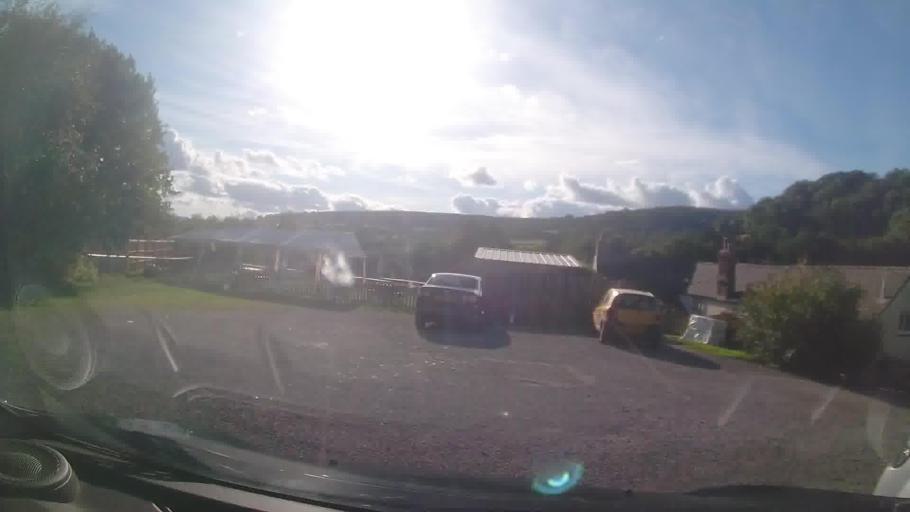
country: GB
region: Wales
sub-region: Blaenau Gwent
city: Brynmawr
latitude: 51.9059
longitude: -3.1914
